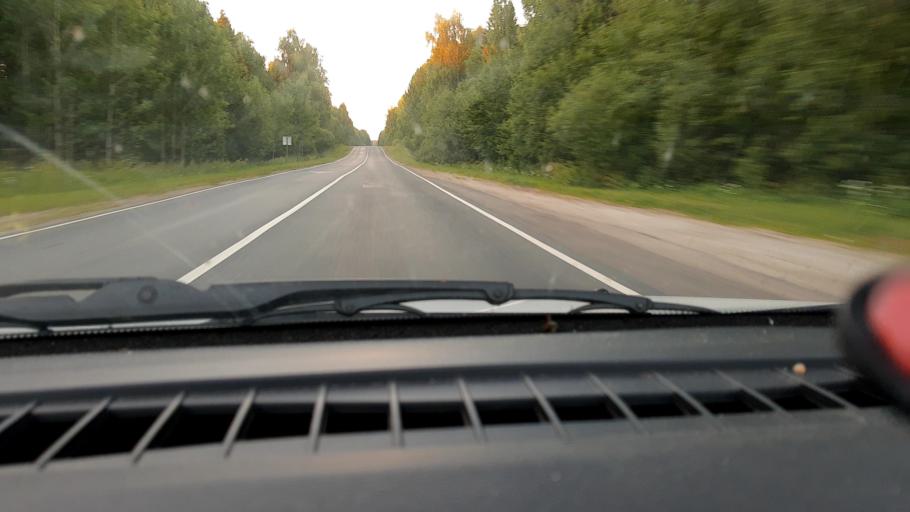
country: RU
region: Nizjnij Novgorod
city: Uren'
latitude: 57.2757
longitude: 45.6323
